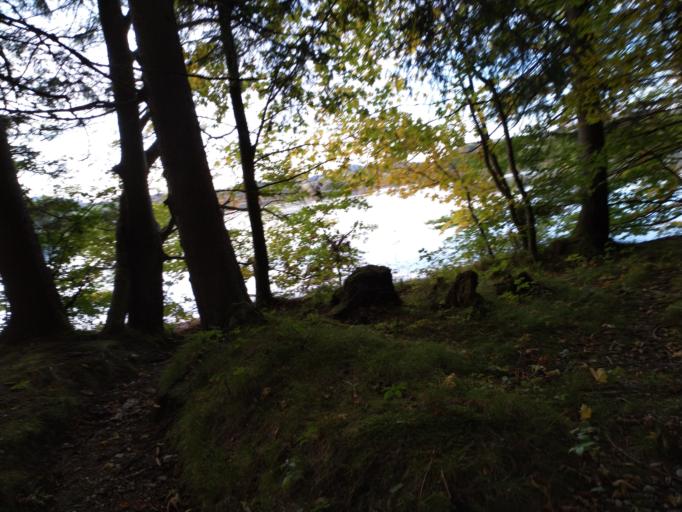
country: AT
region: Tyrol
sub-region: Politischer Bezirk Reutte
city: Vils
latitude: 47.5678
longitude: 10.6418
